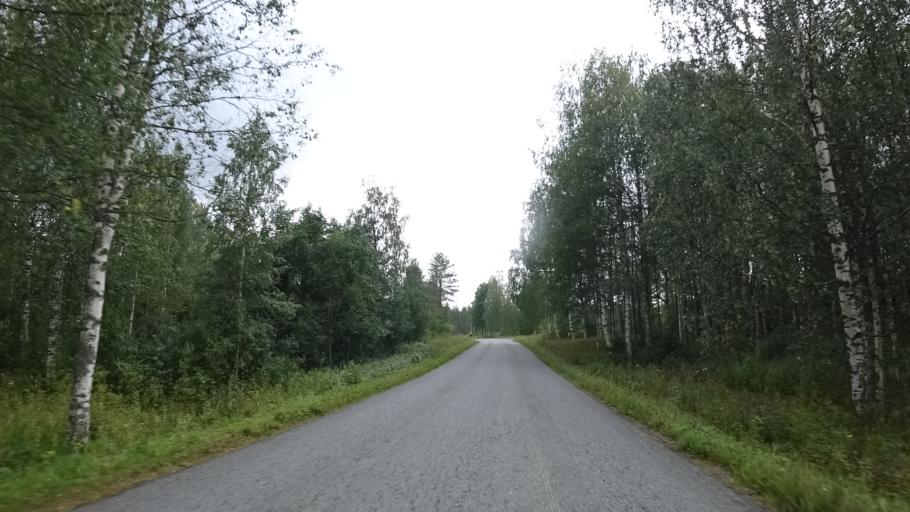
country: FI
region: North Karelia
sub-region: Joensuu
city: Ilomantsi
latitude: 62.9423
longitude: 31.2916
